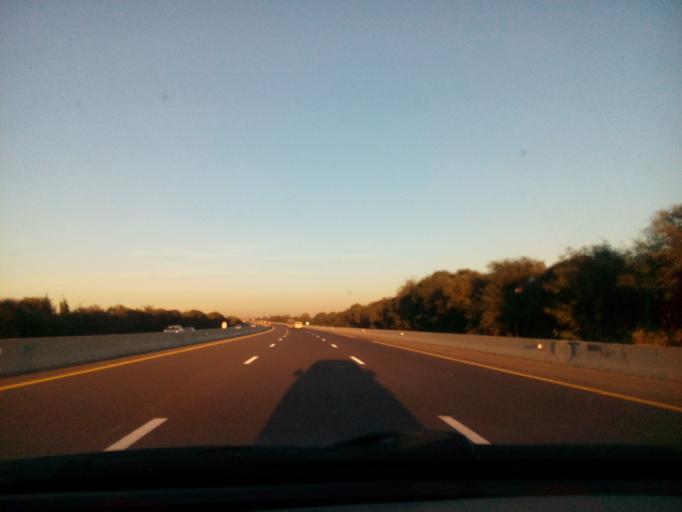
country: DZ
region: Relizane
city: Oued Rhiou
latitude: 36.0097
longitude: 1.0152
